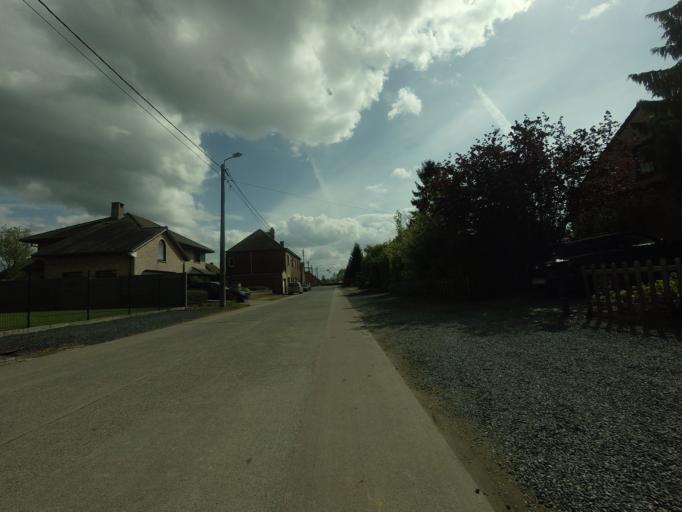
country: BE
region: Flanders
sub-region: Provincie Vlaams-Brabant
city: Zemst
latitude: 51.0142
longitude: 4.4171
